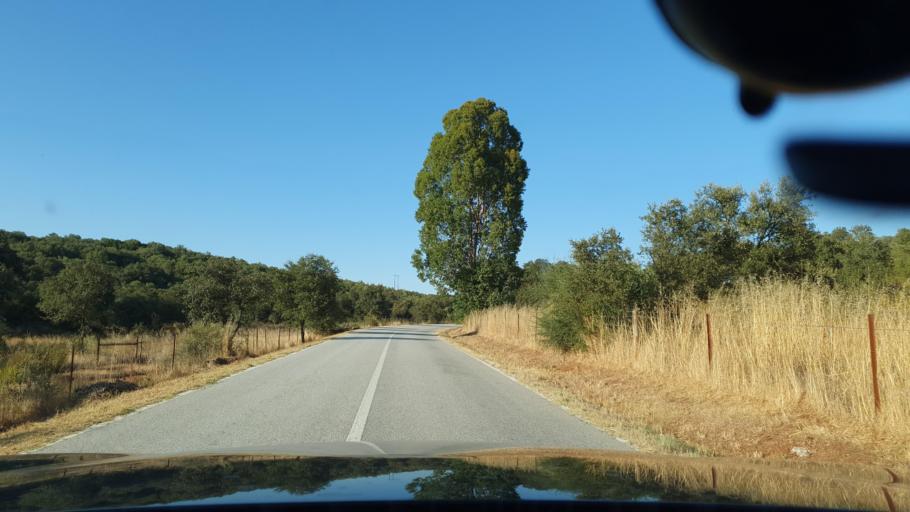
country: PT
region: Evora
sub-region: Estremoz
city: Estremoz
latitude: 38.9067
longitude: -7.6667
